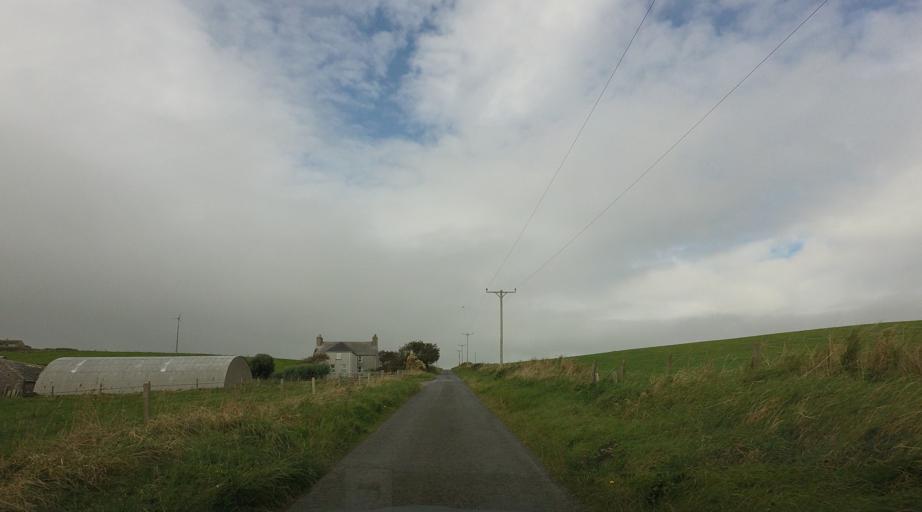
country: GB
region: Scotland
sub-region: Orkney Islands
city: Kirkwall
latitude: 58.8061
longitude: -2.9237
